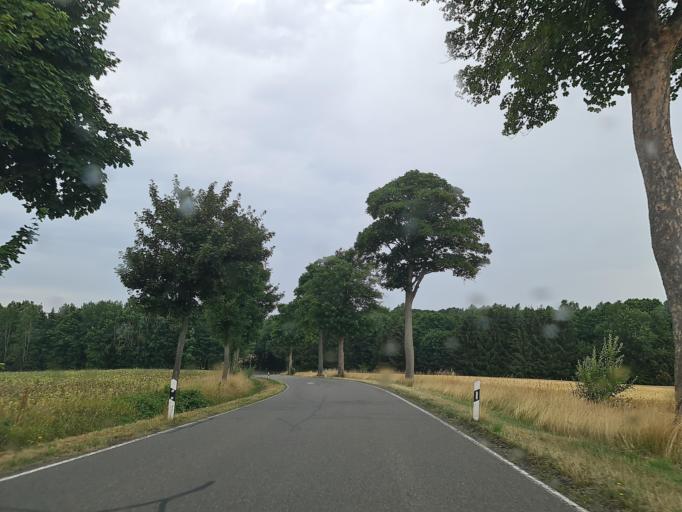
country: DE
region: Saxony
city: Grosshartmannsdorf
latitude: 50.7960
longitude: 13.2939
